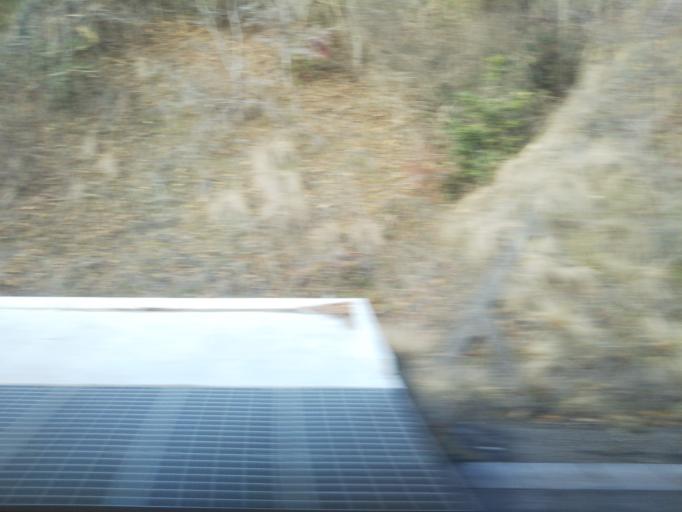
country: JP
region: Kagawa
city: Sakaidecho
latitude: 34.4532
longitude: 133.8072
